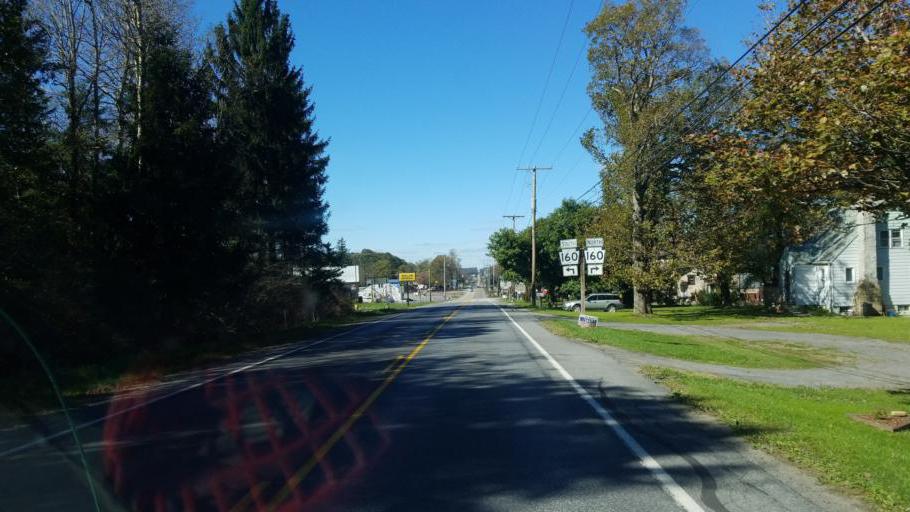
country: US
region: Pennsylvania
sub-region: Somerset County
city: Central City
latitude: 40.0577
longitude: -78.8262
